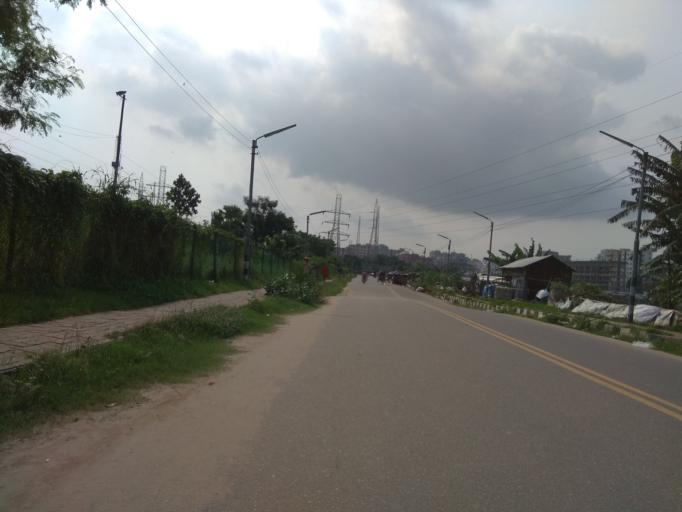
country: BD
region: Dhaka
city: Tungi
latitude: 23.8304
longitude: 90.3568
